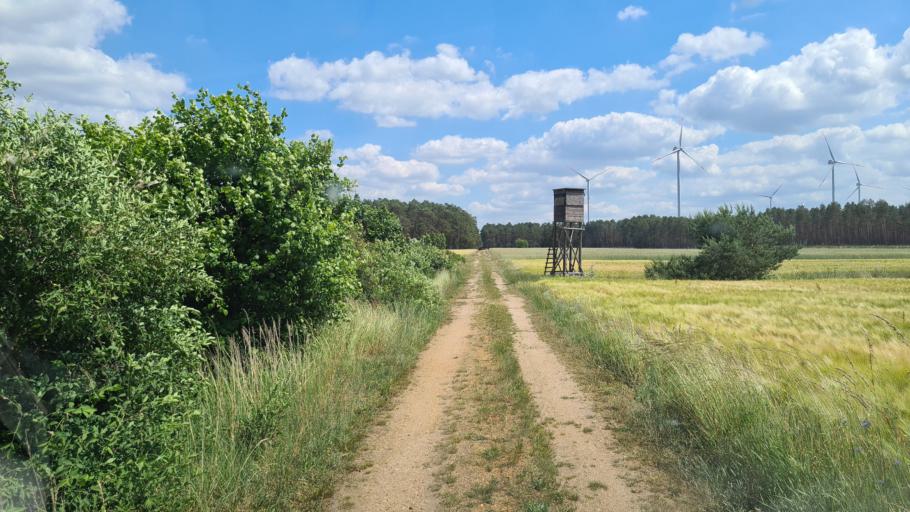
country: DE
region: Brandenburg
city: Sallgast
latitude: 51.6543
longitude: 13.8132
